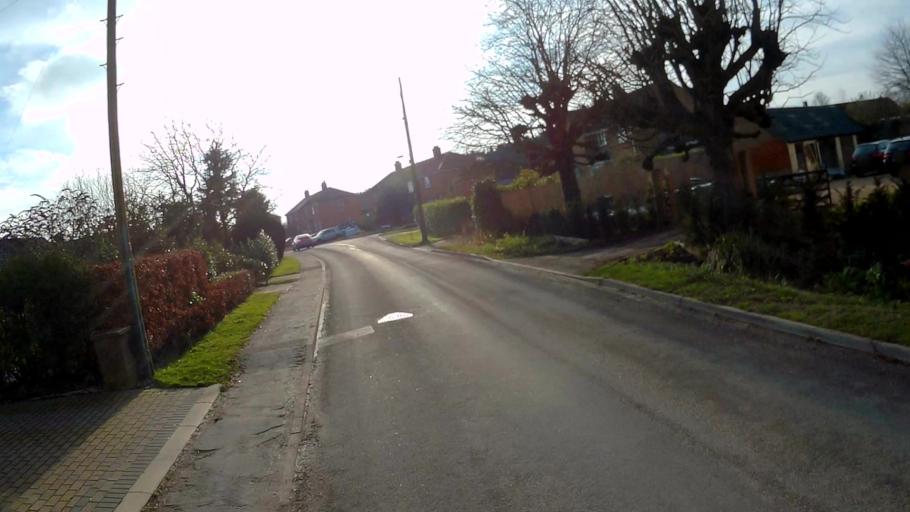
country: GB
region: England
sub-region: Lincolnshire
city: Bourne
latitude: 52.7419
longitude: -0.3831
